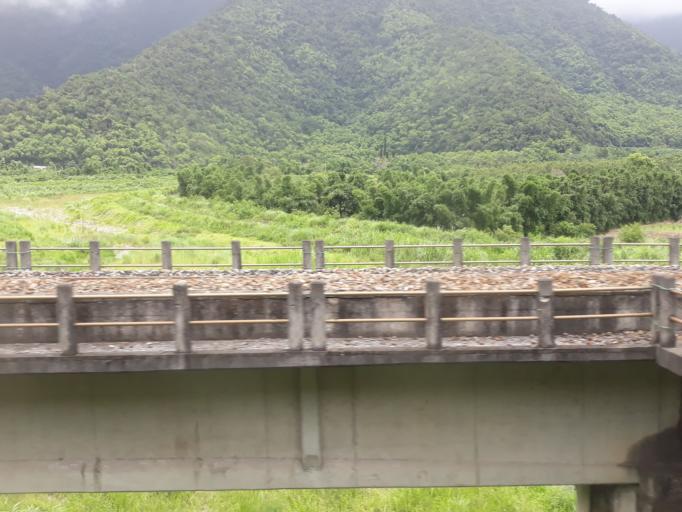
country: TW
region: Taiwan
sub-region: Yilan
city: Yilan
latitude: 24.4620
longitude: 121.8093
